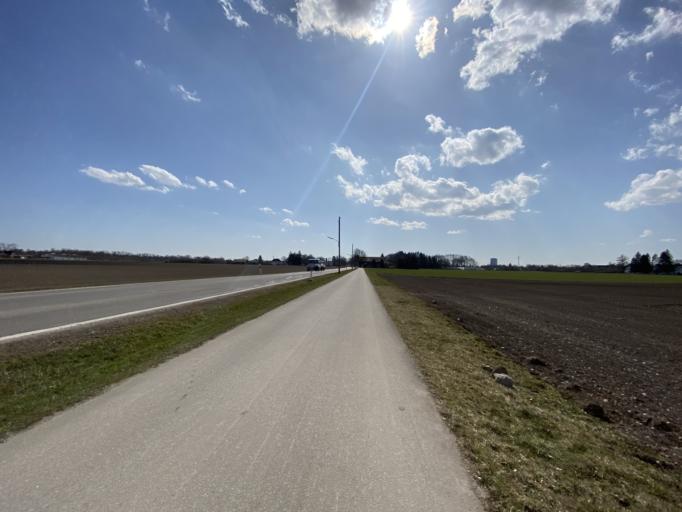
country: DE
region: Bavaria
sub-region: Upper Bavaria
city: Unterfoehring
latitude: 48.1567
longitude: 11.6598
